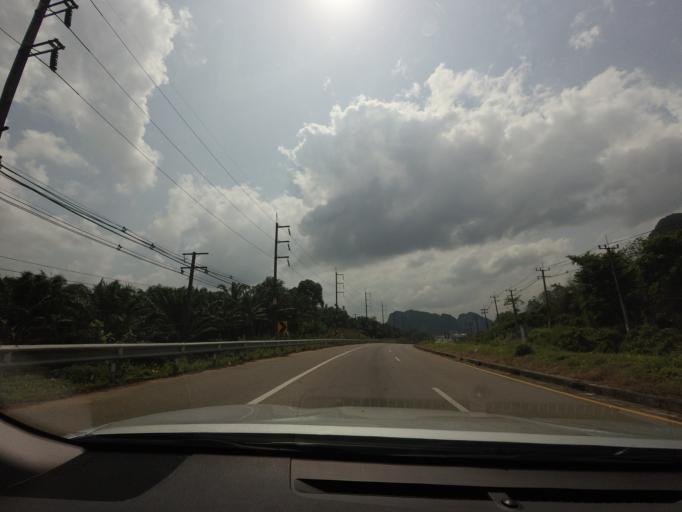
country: TH
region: Krabi
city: Ao Luek
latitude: 8.4064
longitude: 98.7410
